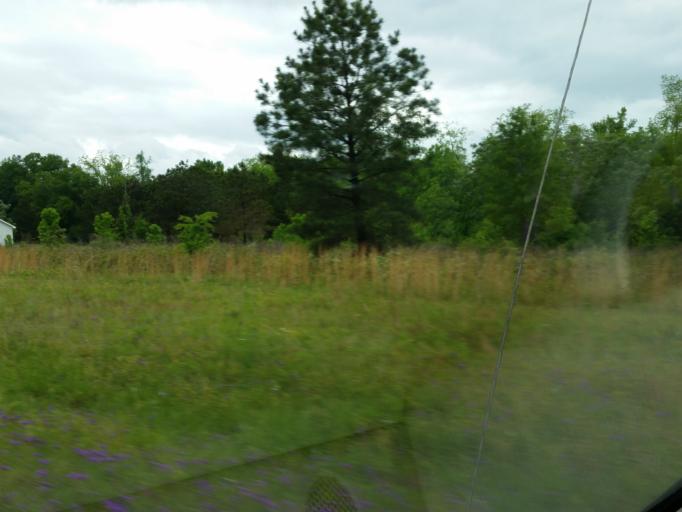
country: US
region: Georgia
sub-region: Peach County
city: Byron
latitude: 32.6800
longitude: -83.8415
